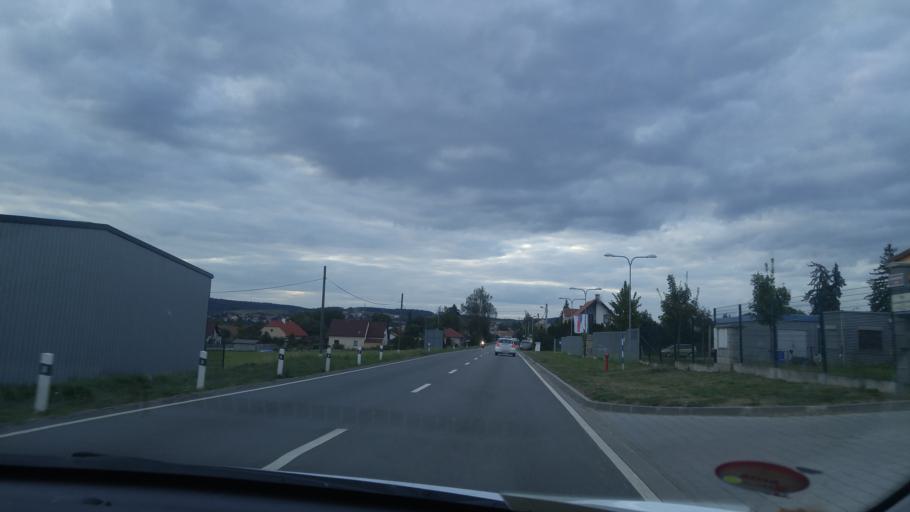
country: CZ
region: South Moravian
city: Ricany
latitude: 49.2047
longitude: 16.4174
